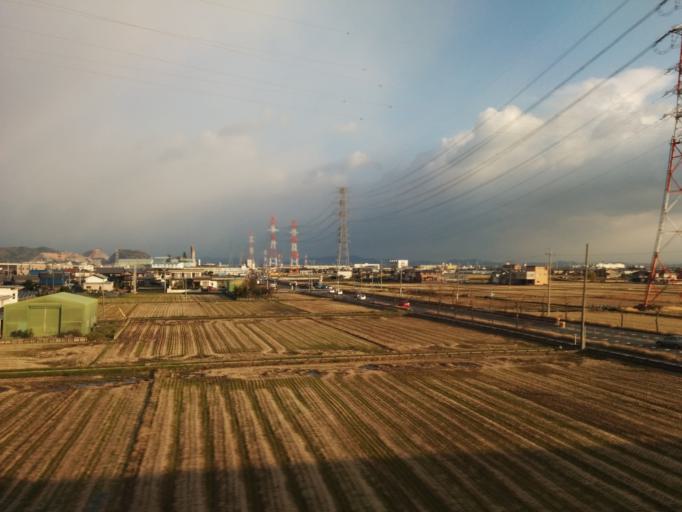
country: JP
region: Gifu
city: Ogaki
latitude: 35.3490
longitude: 136.5827
